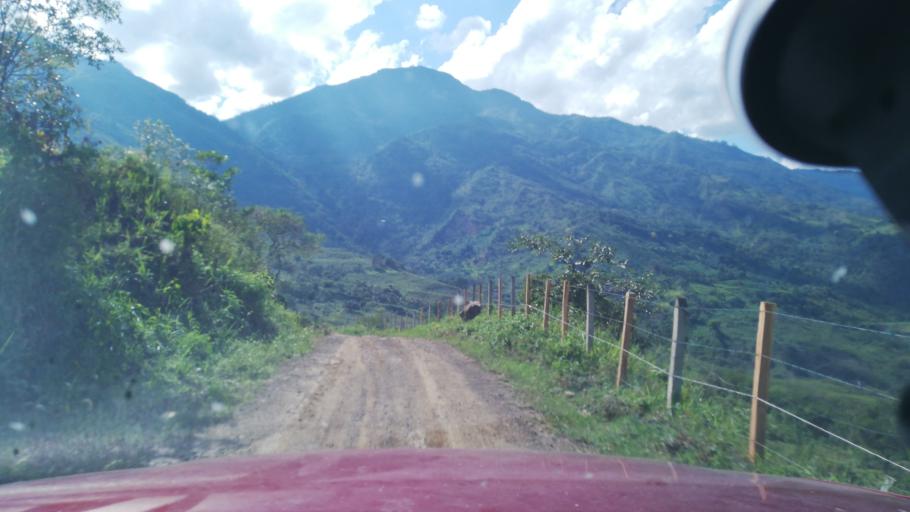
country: CO
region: Cundinamarca
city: Quipile
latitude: 4.7617
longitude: -74.6248
